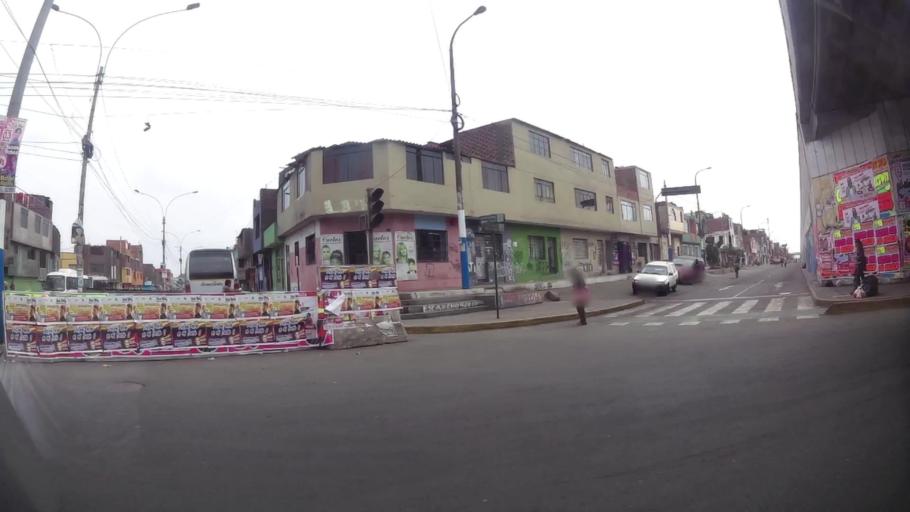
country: PE
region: Callao
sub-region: Callao
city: Callao
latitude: -12.0319
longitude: -77.0776
